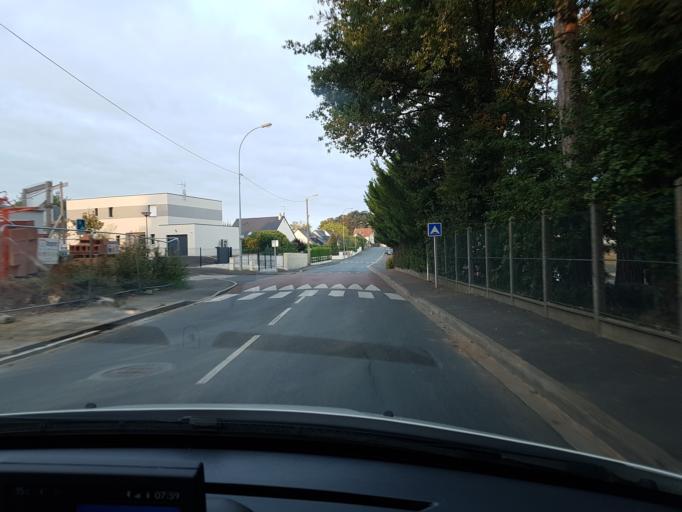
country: FR
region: Centre
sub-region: Departement d'Indre-et-Loire
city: Saint-Avertin
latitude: 47.3597
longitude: 0.7355
